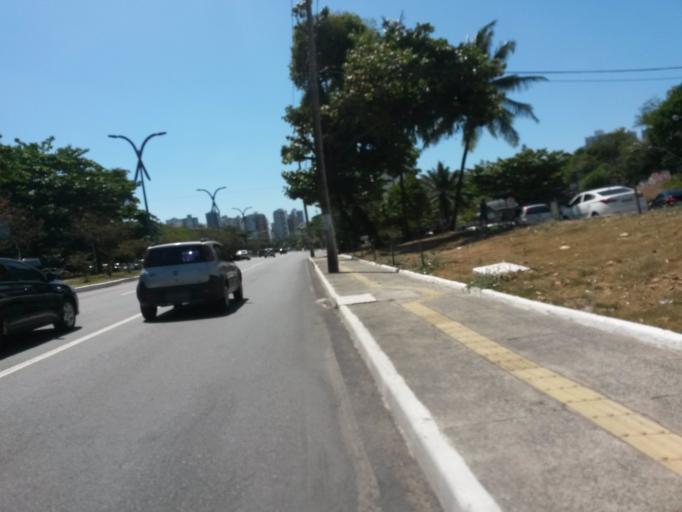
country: BR
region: Bahia
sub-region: Salvador
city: Salvador
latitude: -12.9962
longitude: -38.4678
